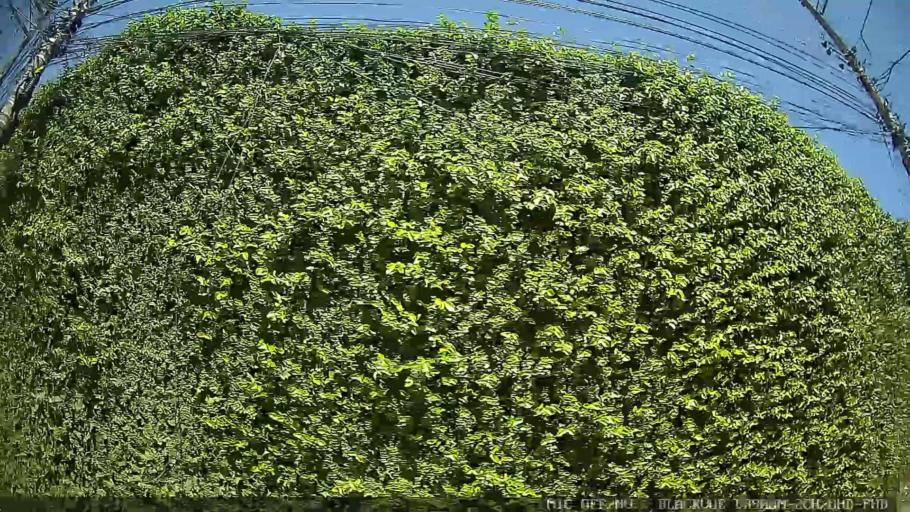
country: BR
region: Sao Paulo
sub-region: Sao Caetano Do Sul
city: Sao Caetano do Sul
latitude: -23.5891
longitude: -46.5205
